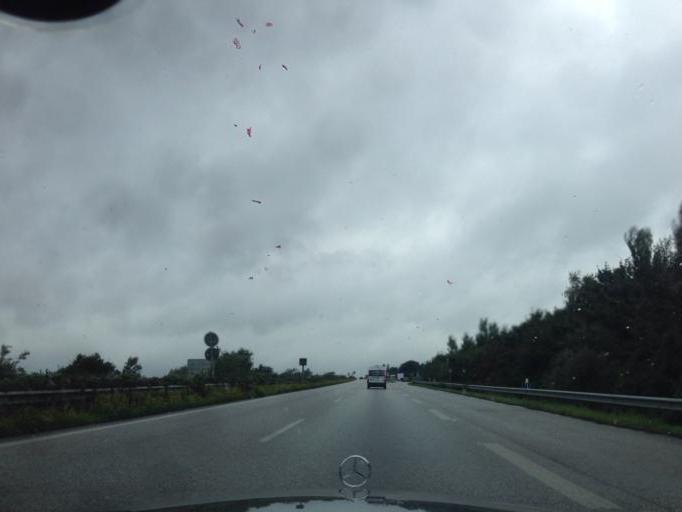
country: DE
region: Schleswig-Holstein
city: Borgstedt
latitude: 54.3241
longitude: 9.7363
